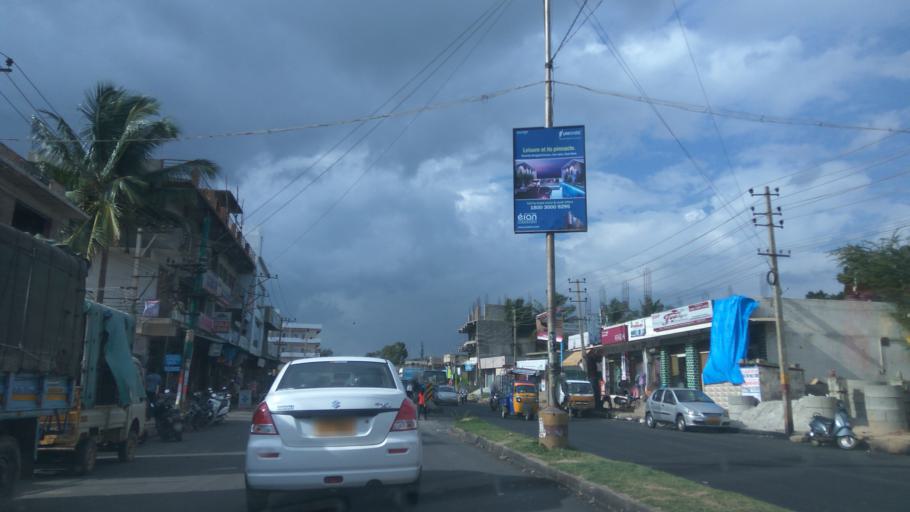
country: IN
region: Karnataka
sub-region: Bangalore Urban
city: Yelahanka
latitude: 13.0527
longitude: 77.6313
